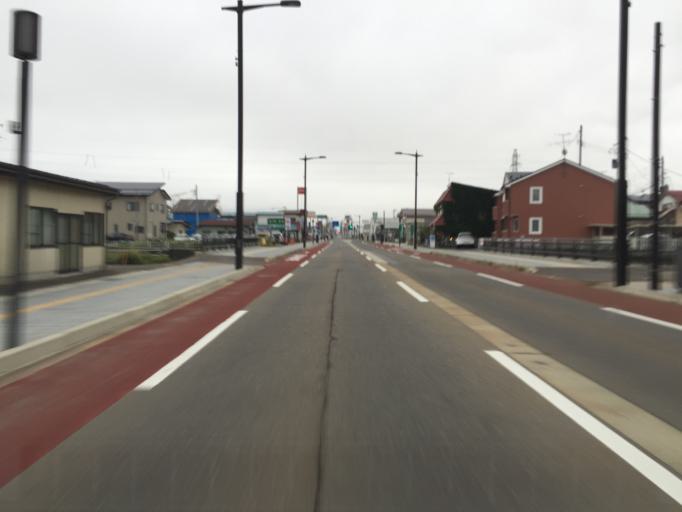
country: JP
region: Fukushima
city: Kitakata
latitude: 37.4809
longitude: 139.9256
